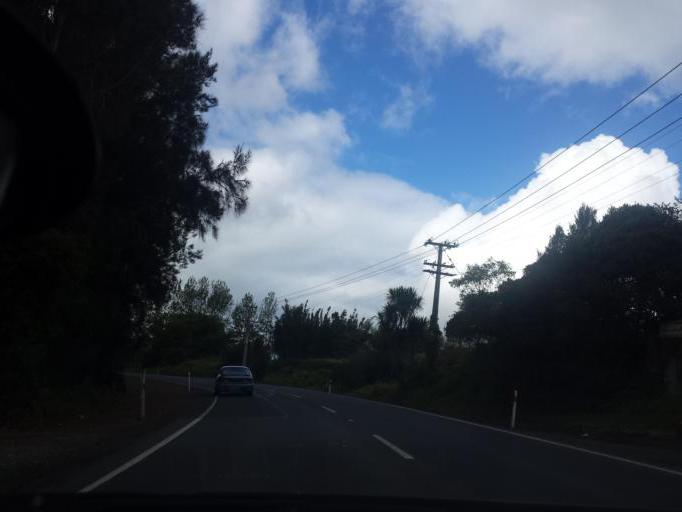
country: NZ
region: Auckland
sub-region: Auckland
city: Warkworth
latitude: -36.3974
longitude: 174.6771
